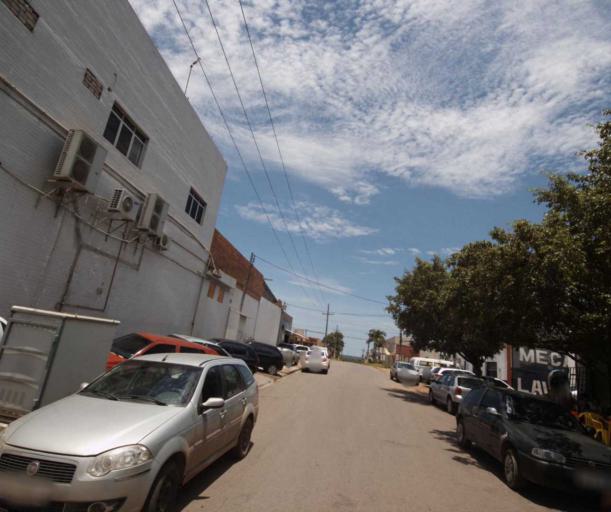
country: BR
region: Mato Grosso
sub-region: Varzea Grande
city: Varzea Grande
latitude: -15.6381
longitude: -56.1213
